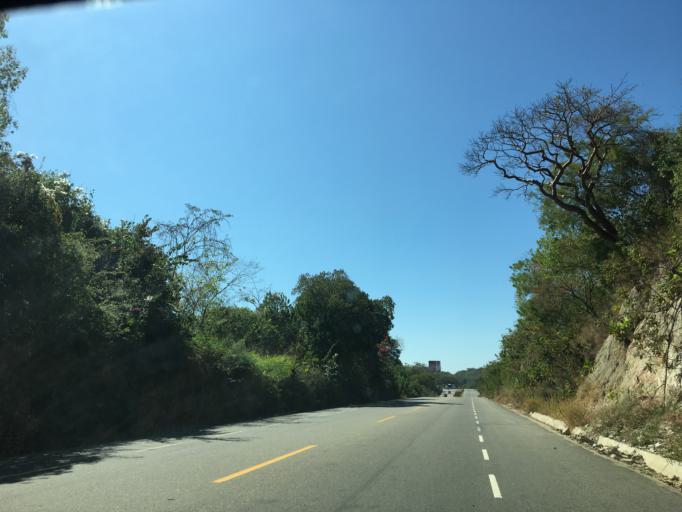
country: MX
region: Oaxaca
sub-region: Santa Maria Huatulco
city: Cuapinolito (Azulillo)
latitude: 15.7698
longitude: -96.2539
